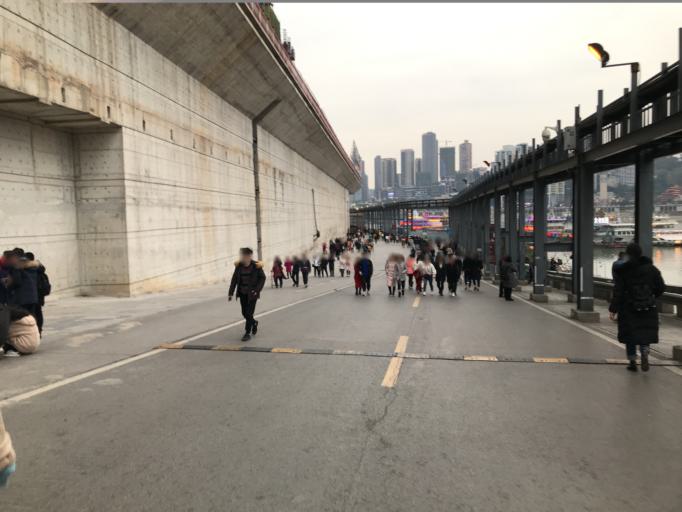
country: CN
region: Chongqing Shi
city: Nanping
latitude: 29.5667
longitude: 106.5855
